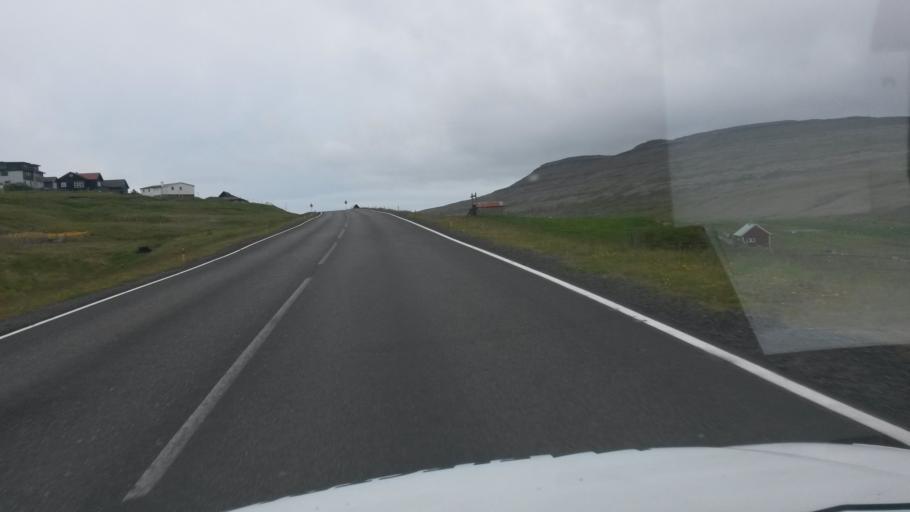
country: FO
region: Streymoy
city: Hoyvik
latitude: 62.0009
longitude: -6.8368
